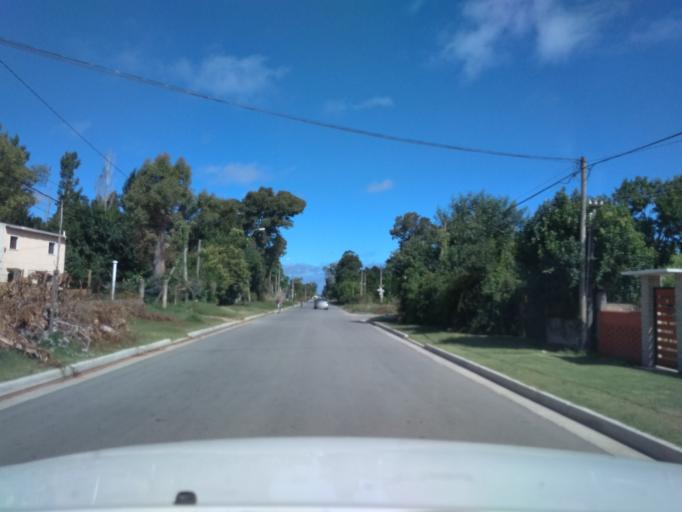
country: UY
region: Canelones
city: Colonia Nicolich
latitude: -34.8217
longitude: -55.9745
